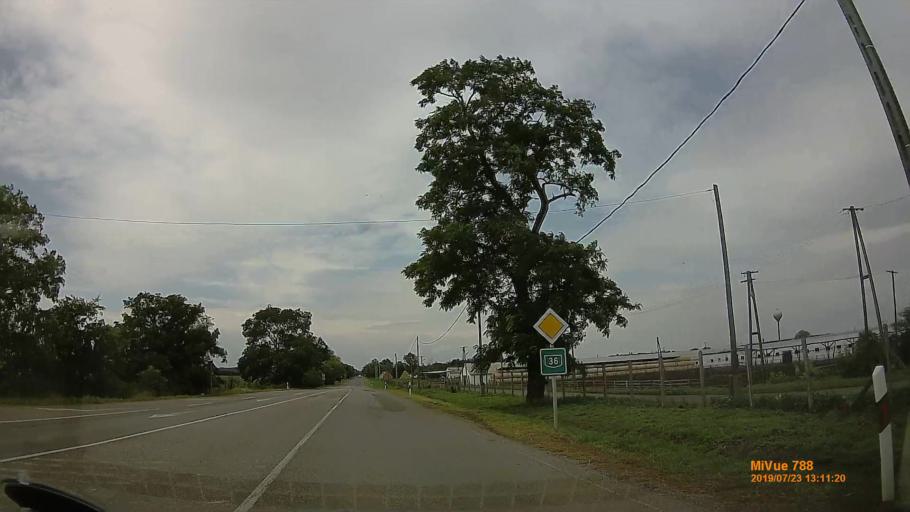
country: HU
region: Szabolcs-Szatmar-Bereg
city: Tiszavasvari
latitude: 47.9278
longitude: 21.2743
